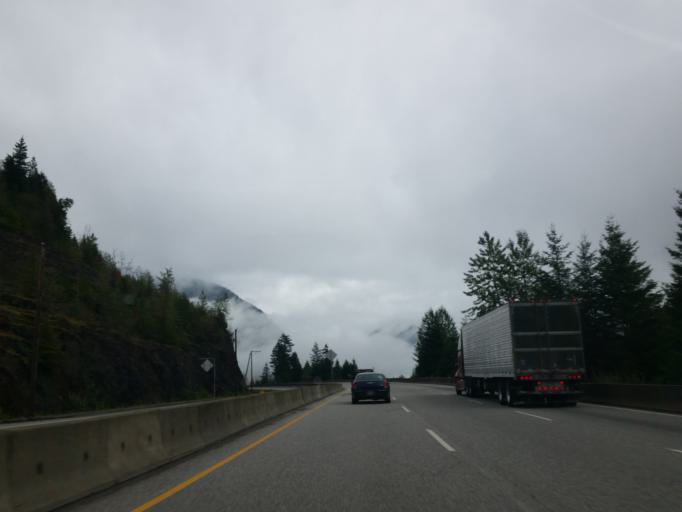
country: CA
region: British Columbia
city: Hope
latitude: 49.4945
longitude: -121.2383
